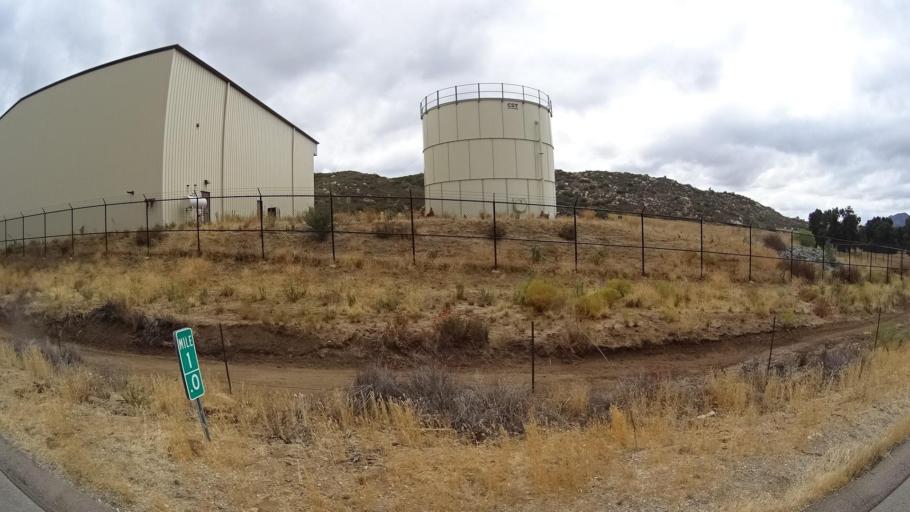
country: US
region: California
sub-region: San Diego County
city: Pine Valley
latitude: 32.7277
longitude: -116.4611
